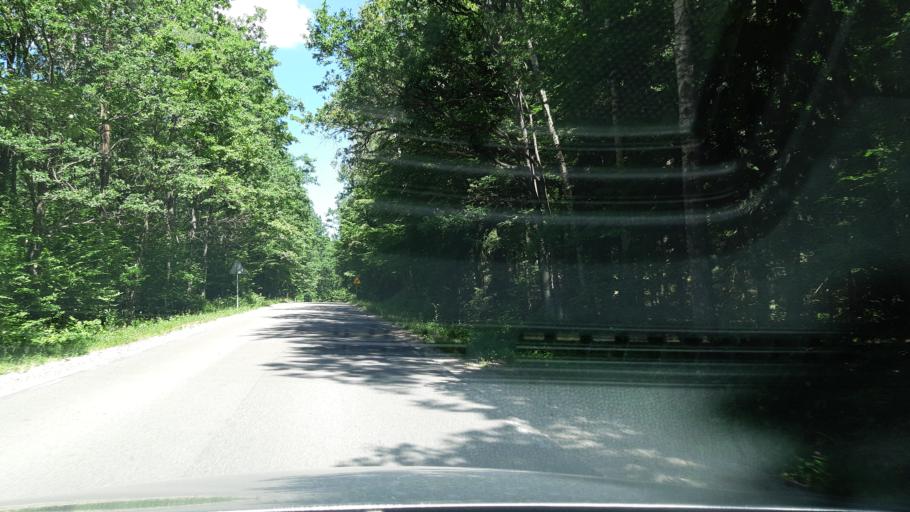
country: PL
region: Warmian-Masurian Voivodeship
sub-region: Powiat piski
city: Ruciane-Nida
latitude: 53.7203
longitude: 21.4959
